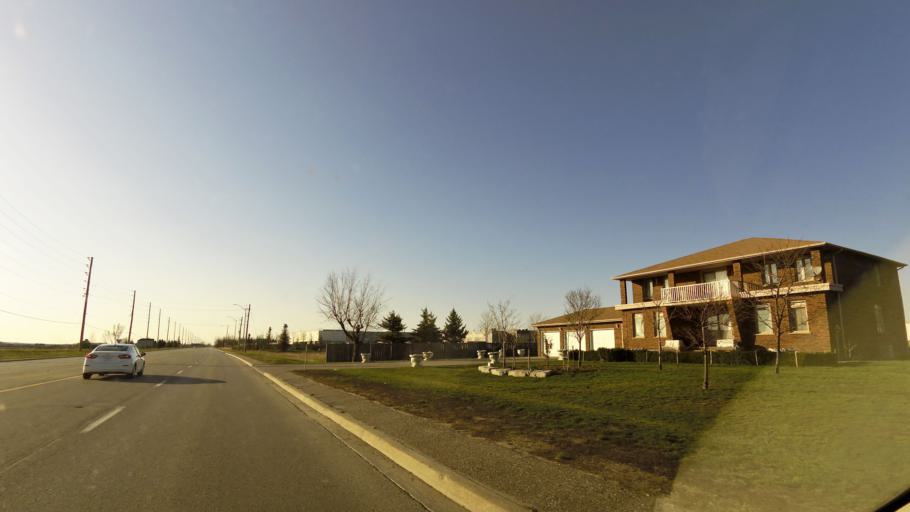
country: CA
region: Ontario
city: Brampton
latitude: 43.8433
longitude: -79.7115
